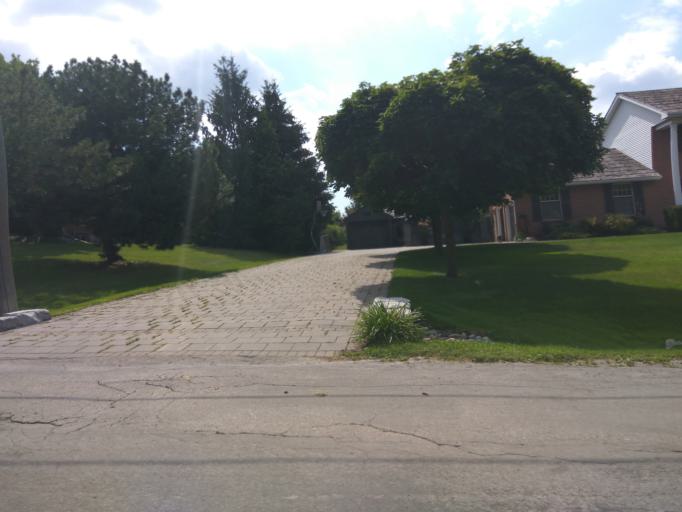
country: CA
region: Ontario
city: Cambridge
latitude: 43.4056
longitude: -80.4008
